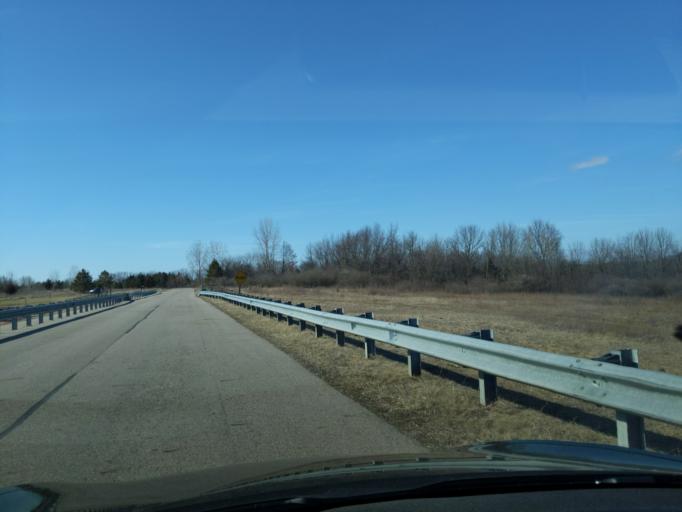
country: US
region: Michigan
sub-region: Ionia County
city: Ionia
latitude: 42.9450
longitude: -85.1268
